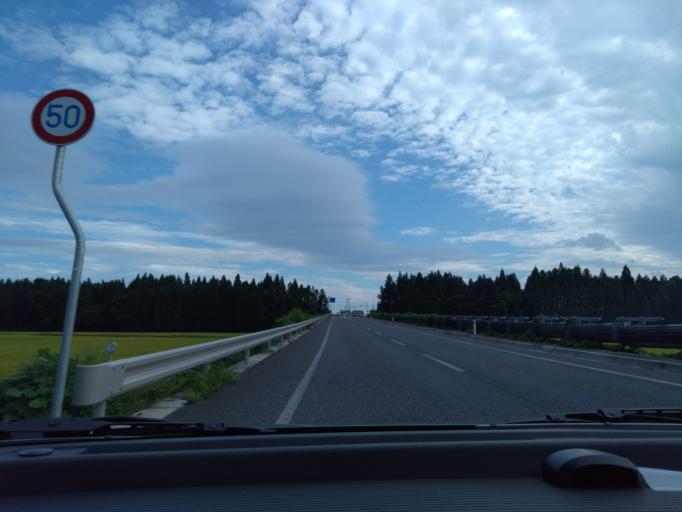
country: JP
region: Iwate
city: Hanamaki
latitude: 39.3764
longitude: 141.0564
